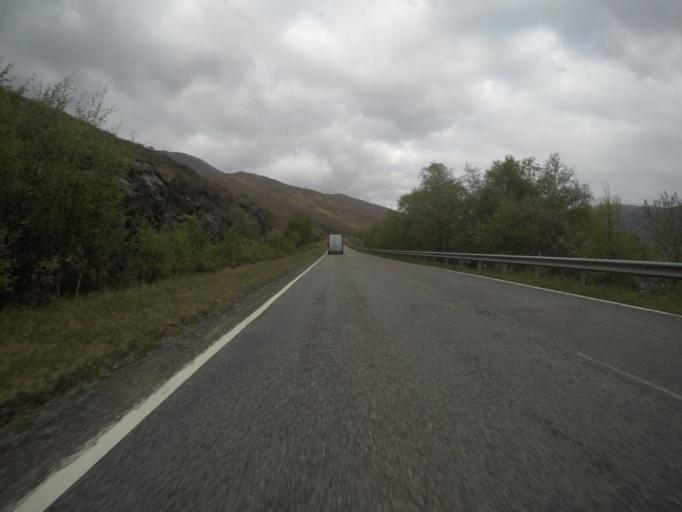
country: GB
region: Scotland
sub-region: Highland
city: Spean Bridge
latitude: 57.1464
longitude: -5.1078
